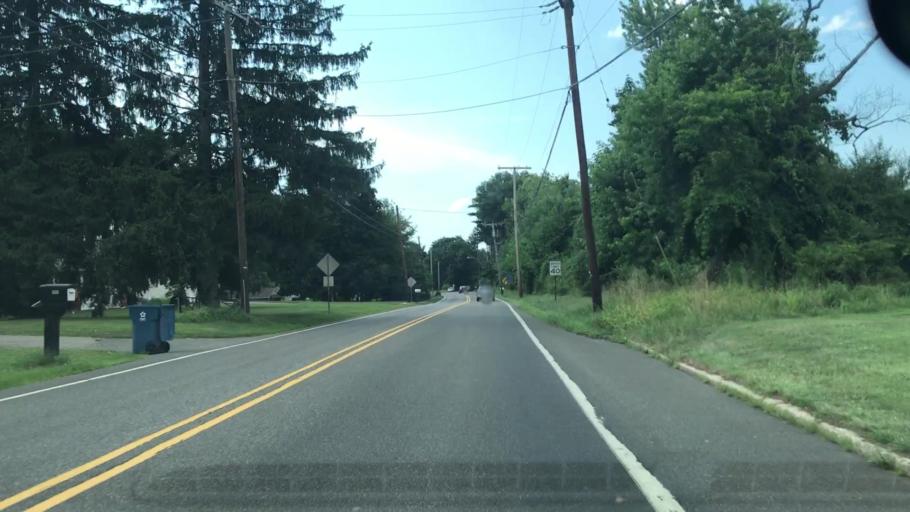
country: US
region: New Jersey
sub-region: Hunterdon County
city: Flemington
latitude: 40.5009
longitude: -74.8080
